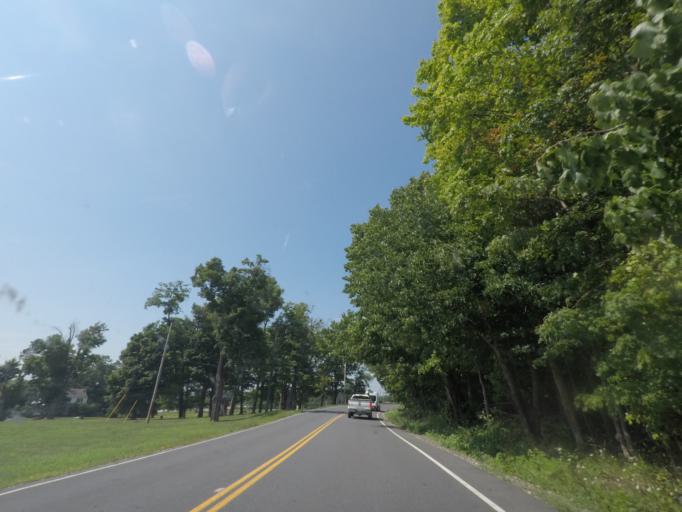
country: US
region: New York
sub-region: Albany County
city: Menands
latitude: 42.6690
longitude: -73.6875
